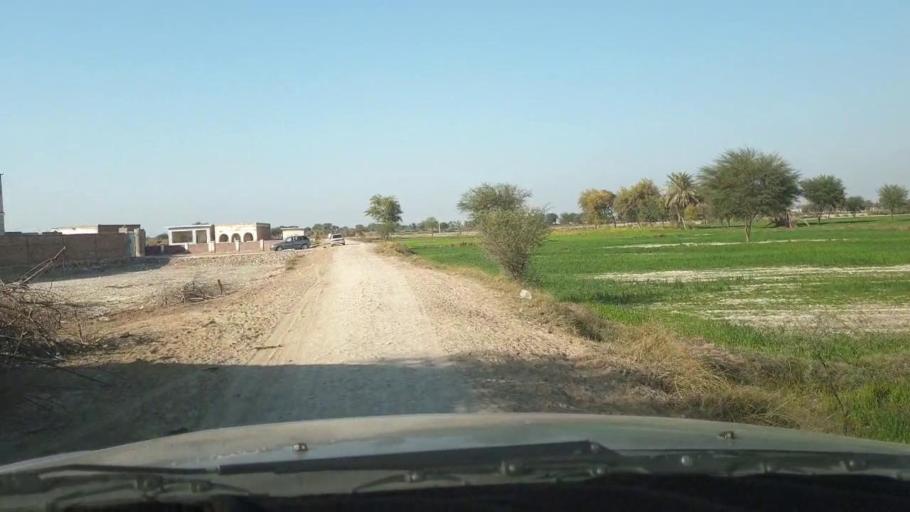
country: PK
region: Sindh
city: Mirpur Mathelo
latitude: 27.9817
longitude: 69.5360
